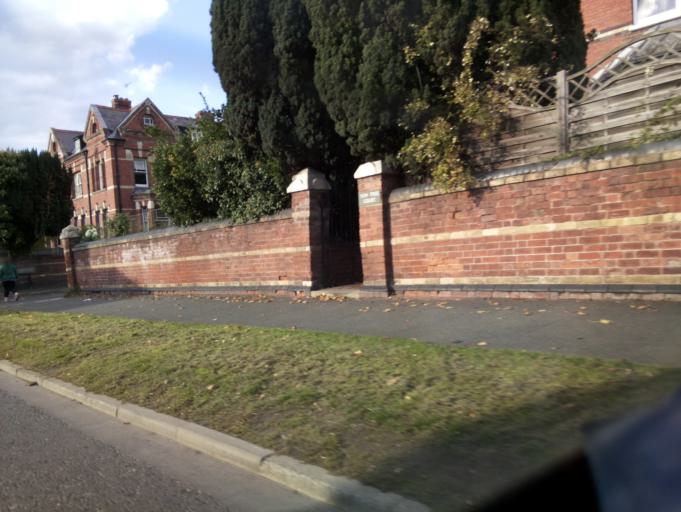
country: GB
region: England
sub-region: Herefordshire
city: Belmont
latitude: 52.0605
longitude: -2.7362
